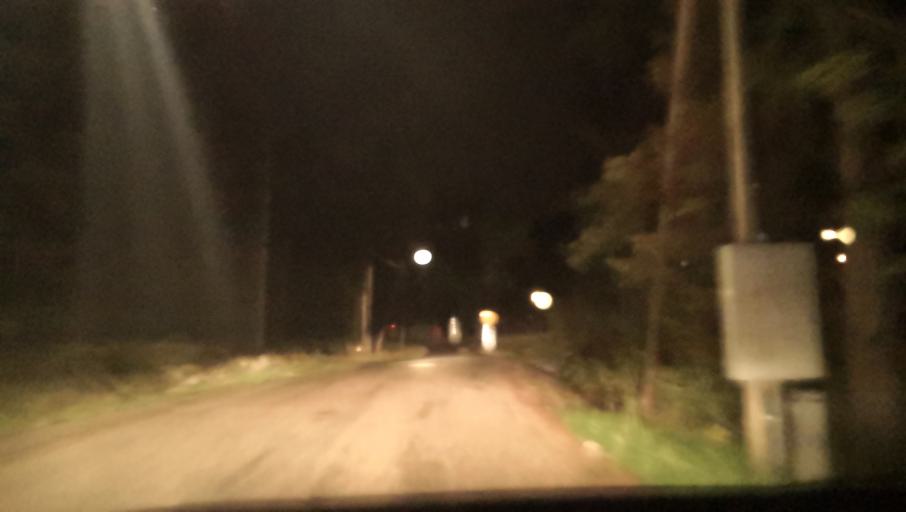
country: SE
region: Stockholm
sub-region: Nacka Kommun
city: Boo
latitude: 59.3289
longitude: 18.3209
